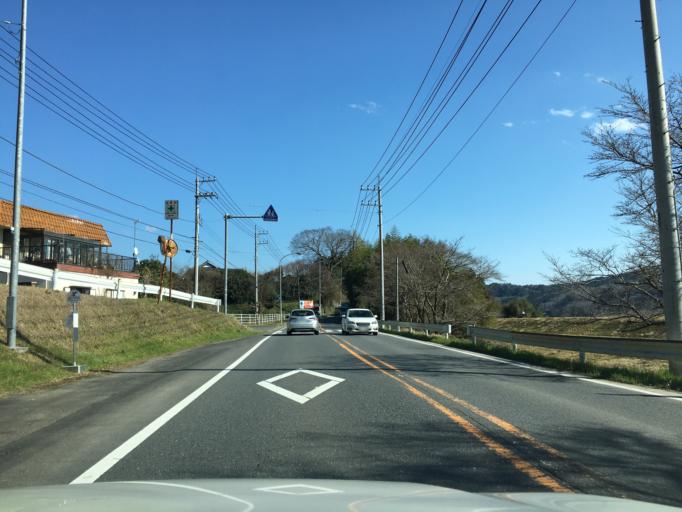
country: JP
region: Ibaraki
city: Omiya
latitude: 36.5639
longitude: 140.3053
